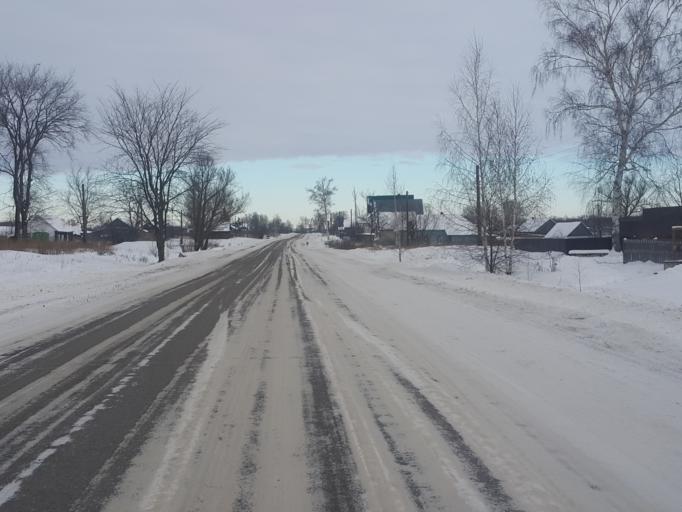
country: RU
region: Tambov
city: Platonovka
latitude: 52.8745
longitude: 41.8727
